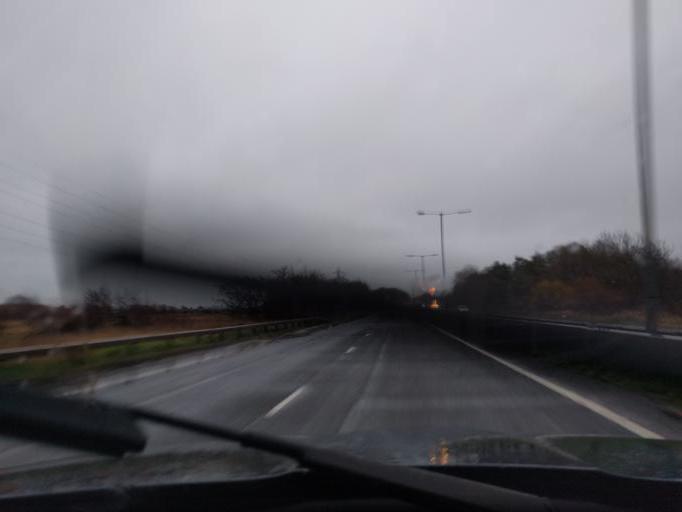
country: GB
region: England
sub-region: Northumberland
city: Newbiggin-by-the-Sea
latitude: 55.1817
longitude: -1.5347
